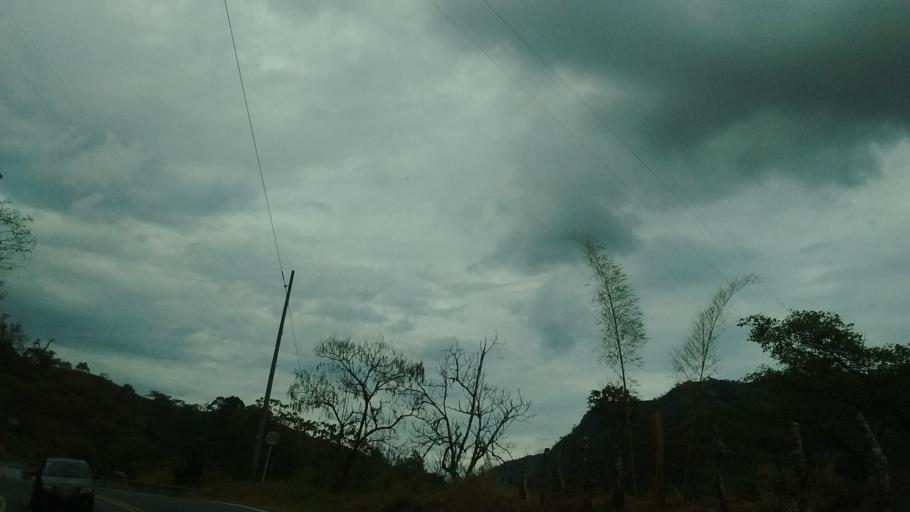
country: CO
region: Cauca
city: Rosas
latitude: 2.2674
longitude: -76.7340
